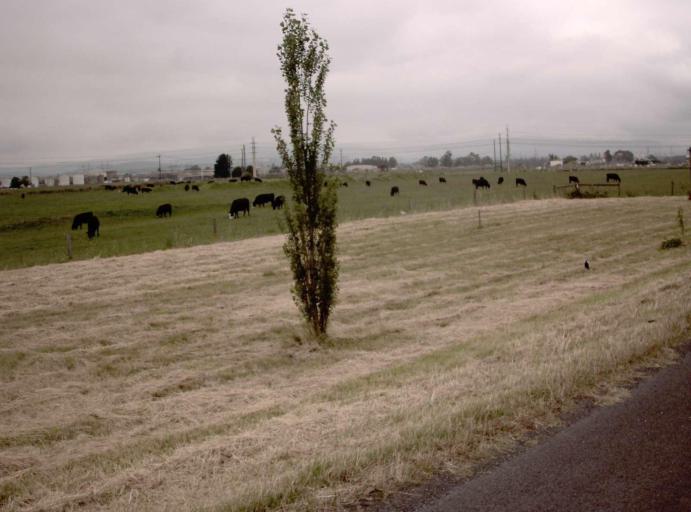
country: AU
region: Victoria
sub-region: Latrobe
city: Morwell
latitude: -38.2511
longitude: 146.4261
